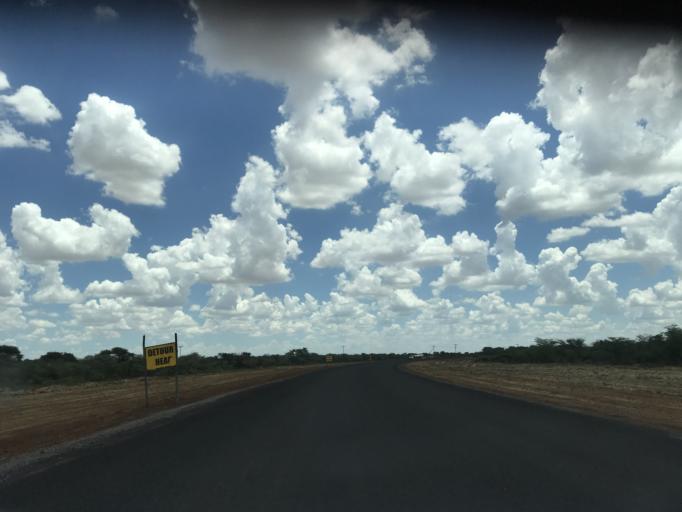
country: BW
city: Mabuli
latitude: -25.8052
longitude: 24.6785
